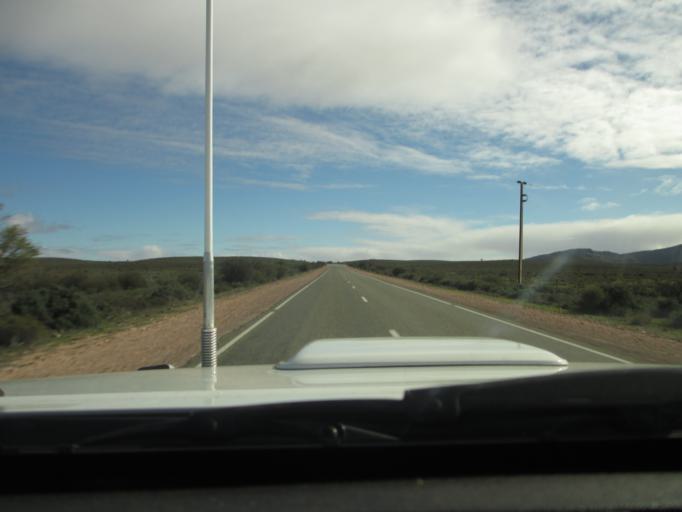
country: AU
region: South Australia
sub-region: Flinders Ranges
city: Quorn
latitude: -31.8176
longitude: 138.3749
